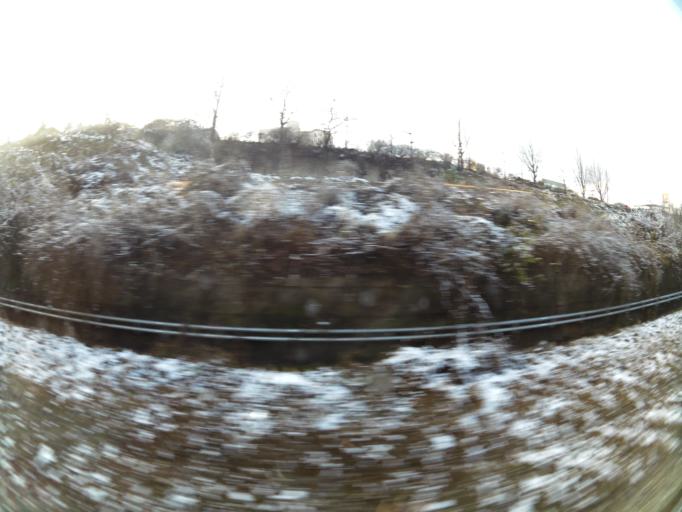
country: KR
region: Daejeon
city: Daejeon
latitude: 36.3630
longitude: 127.4188
